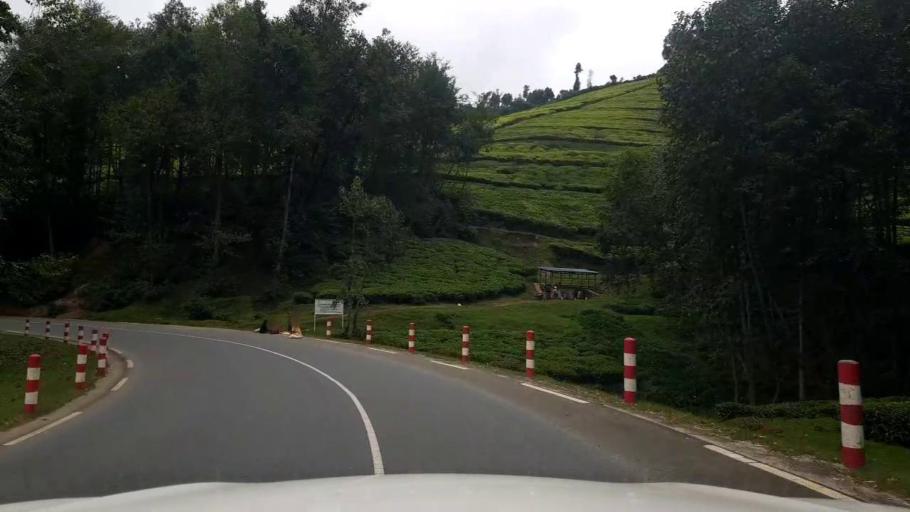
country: RW
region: Northern Province
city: Musanze
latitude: -1.6554
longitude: 29.5092
